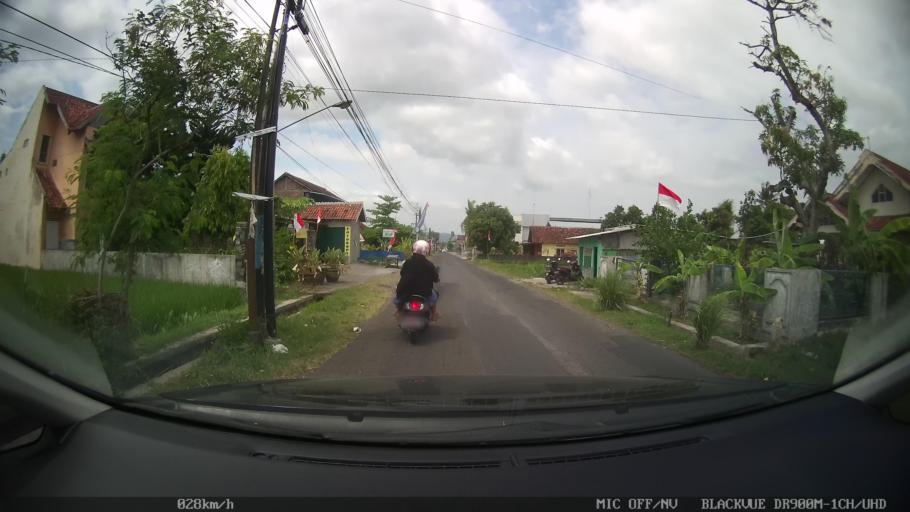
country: ID
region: Daerah Istimewa Yogyakarta
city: Depok
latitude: -7.7812
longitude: 110.4640
